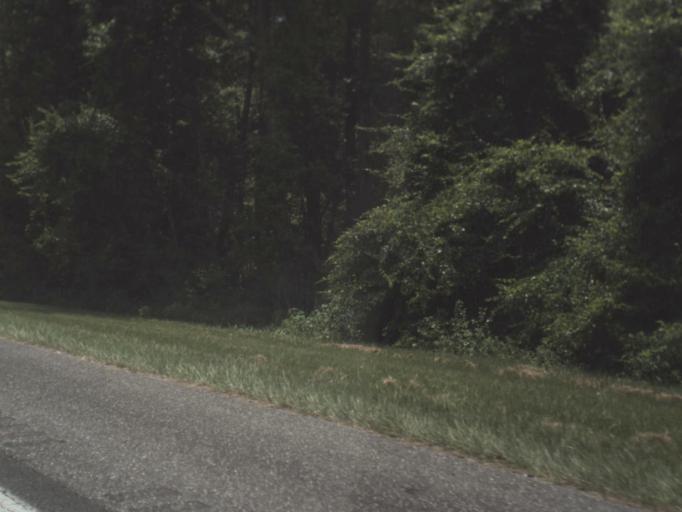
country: US
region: Florida
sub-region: Madison County
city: Madison
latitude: 30.4316
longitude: -83.5493
